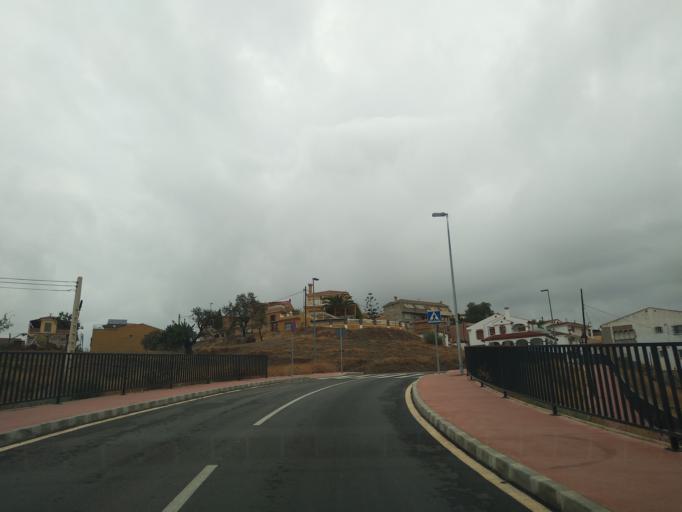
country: ES
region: Andalusia
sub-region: Provincia de Malaga
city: Malaga
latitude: 36.7446
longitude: -4.4790
